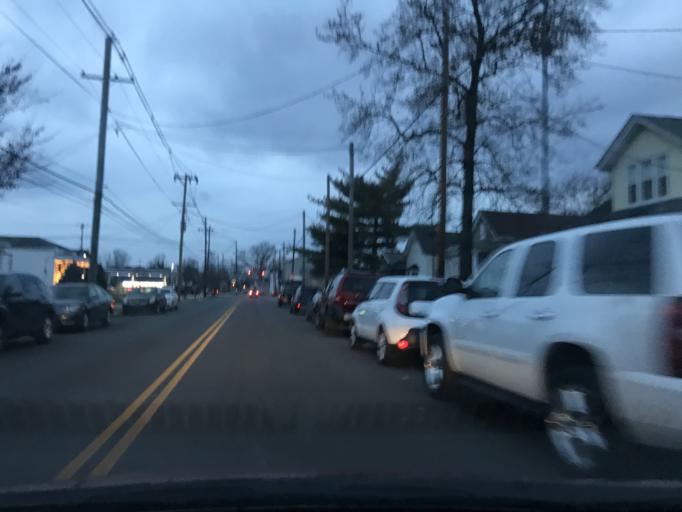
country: US
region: Kentucky
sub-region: Jefferson County
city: Audubon Park
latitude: 38.2240
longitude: -85.7410
